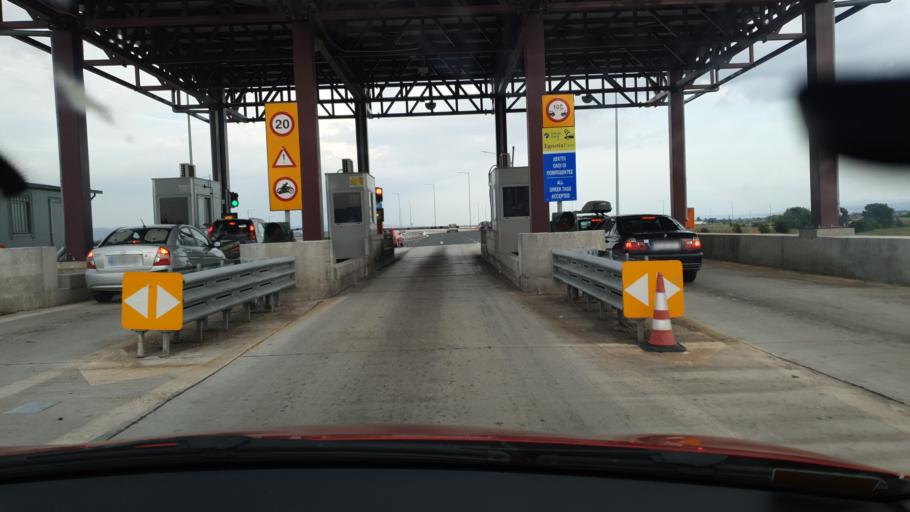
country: GR
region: Central Macedonia
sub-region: Nomos Thessalonikis
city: Lagyna
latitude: 40.7374
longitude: 23.0076
